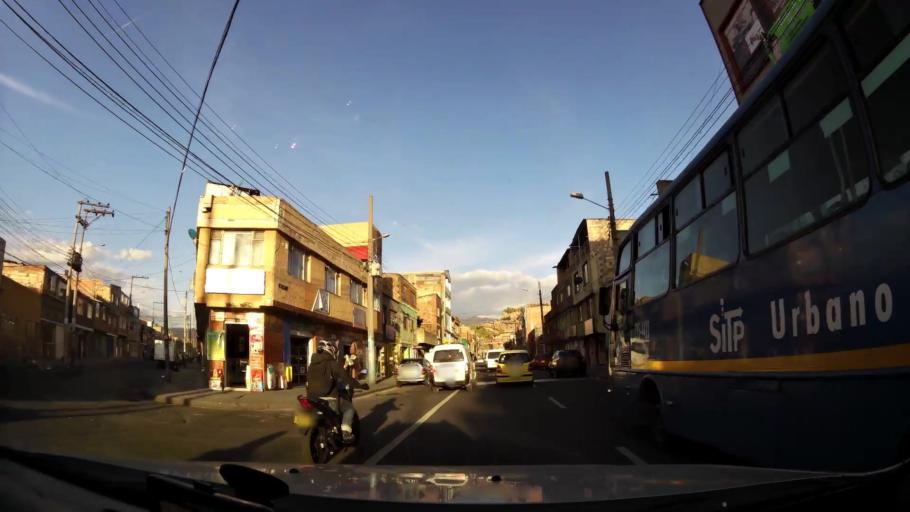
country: CO
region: Bogota D.C.
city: Bogota
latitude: 4.5671
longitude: -74.1290
